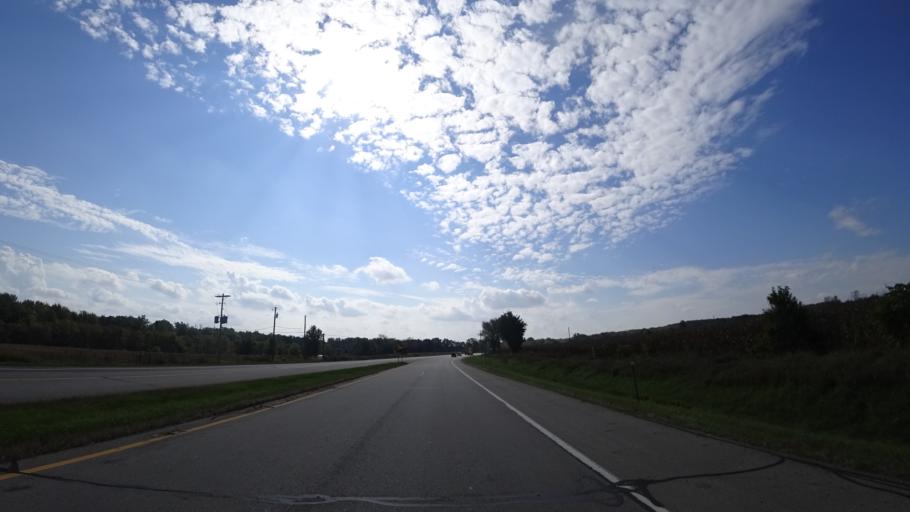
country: US
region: Michigan
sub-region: Saint Joseph County
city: Three Rivers
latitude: 41.9232
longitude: -85.6516
